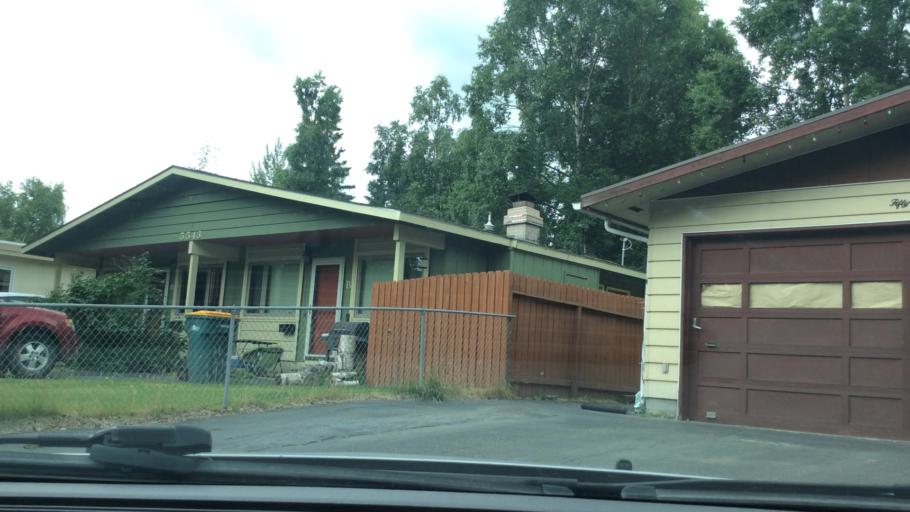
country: US
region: Alaska
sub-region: Anchorage Municipality
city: Anchorage
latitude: 61.2009
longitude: -149.7760
